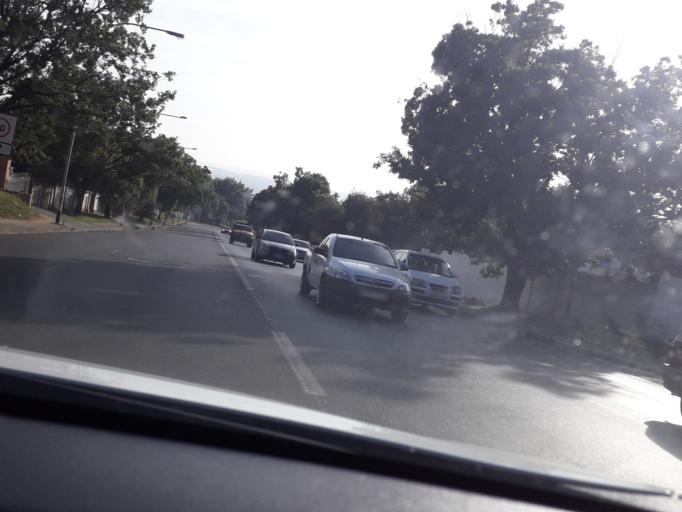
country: ZA
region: Gauteng
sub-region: City of Johannesburg Metropolitan Municipality
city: Johannesburg
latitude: -26.1347
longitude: 28.0940
